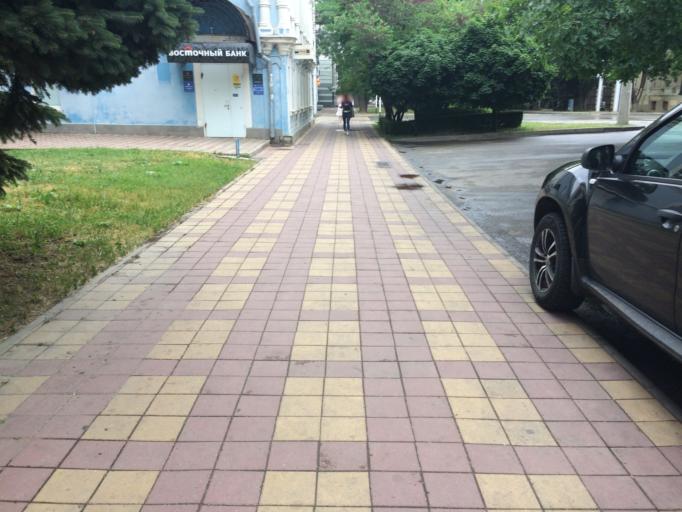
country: RU
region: Stavropol'skiy
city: Stavropol'
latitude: 45.0393
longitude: 41.9652
